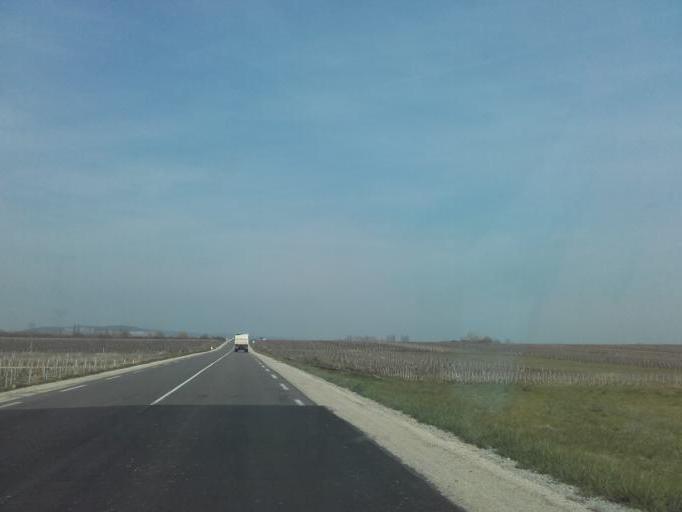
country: FR
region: Bourgogne
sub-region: Departement de la Cote-d'Or
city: Corpeau
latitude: 46.9485
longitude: 4.7630
